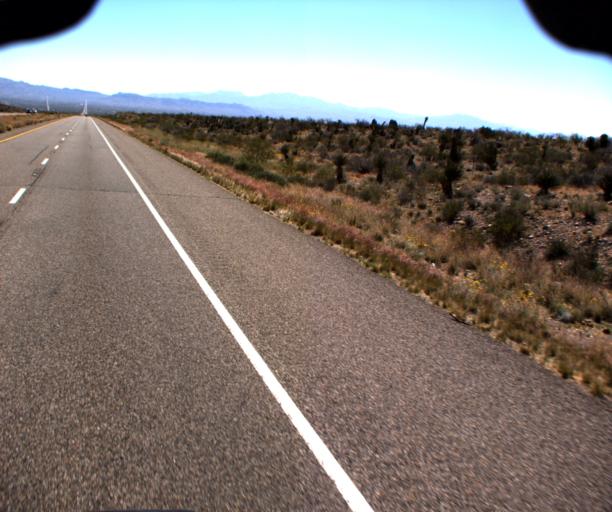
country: US
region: Arizona
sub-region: Mohave County
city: Golden Valley
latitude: 35.2290
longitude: -114.3642
